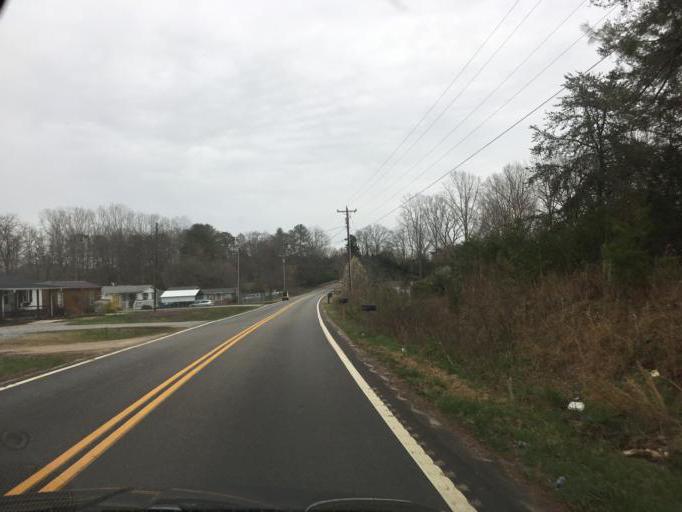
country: US
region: South Carolina
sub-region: Greenville County
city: Berea
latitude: 34.9309
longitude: -82.4976
